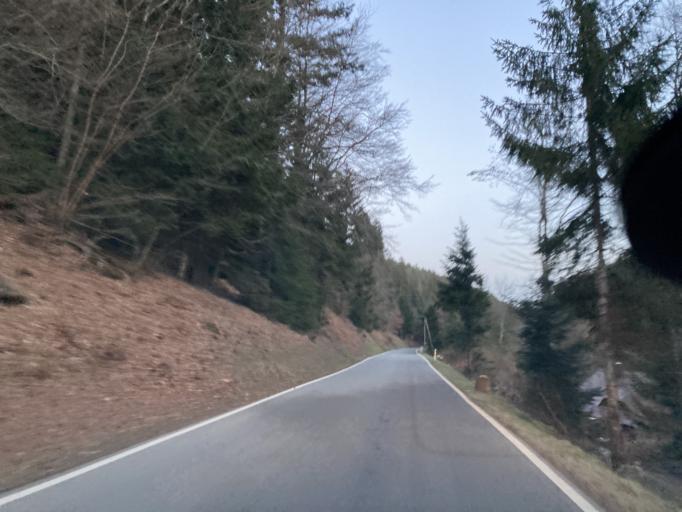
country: DE
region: Baden-Wuerttemberg
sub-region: Karlsruhe Region
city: Bad Teinach-Zavelstein
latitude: 48.6802
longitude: 8.6463
